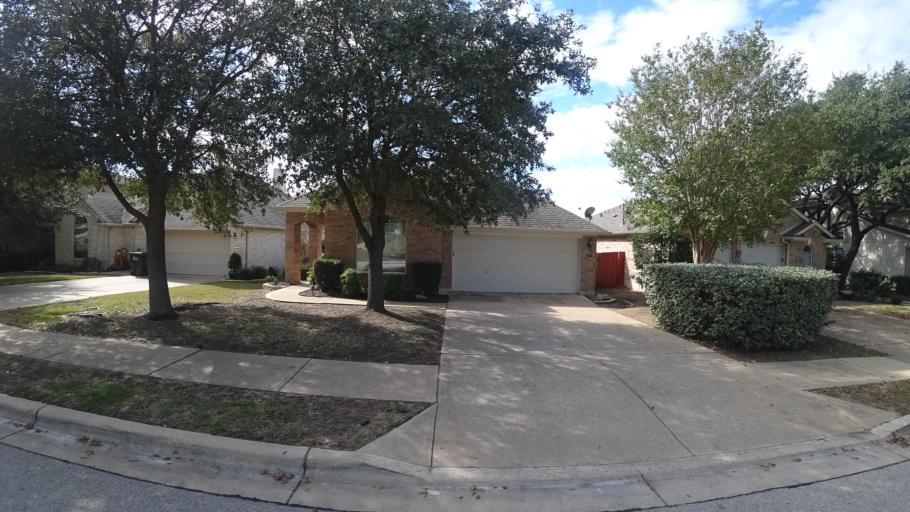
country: US
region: Texas
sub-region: Travis County
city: Hudson Bend
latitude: 30.3643
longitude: -97.9052
